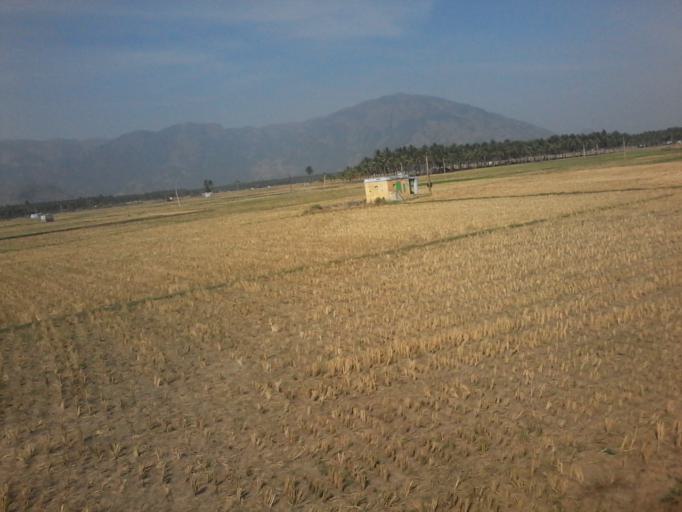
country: IN
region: Tamil Nadu
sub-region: Virudhunagar
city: Srivilliputhur
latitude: 9.6424
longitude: 77.6041
